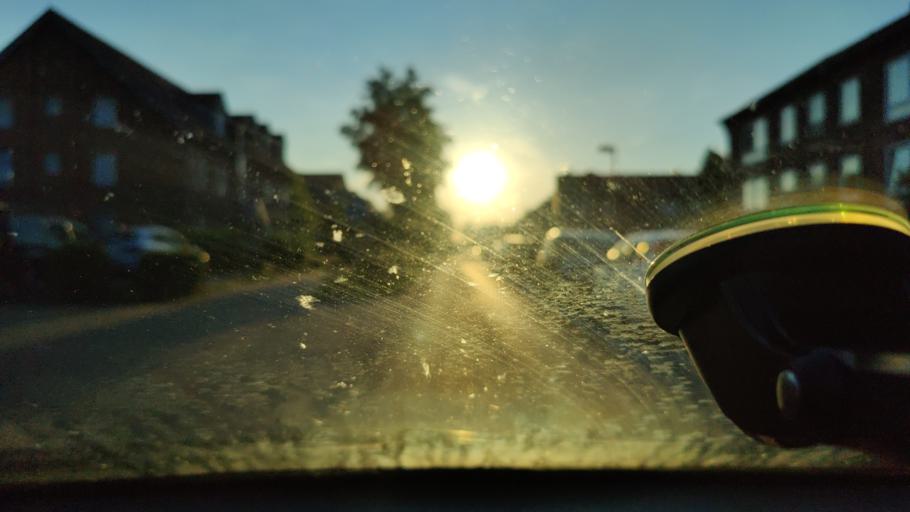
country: DE
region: North Rhine-Westphalia
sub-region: Regierungsbezirk Dusseldorf
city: Kranenburg
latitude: 51.7860
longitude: 6.0110
